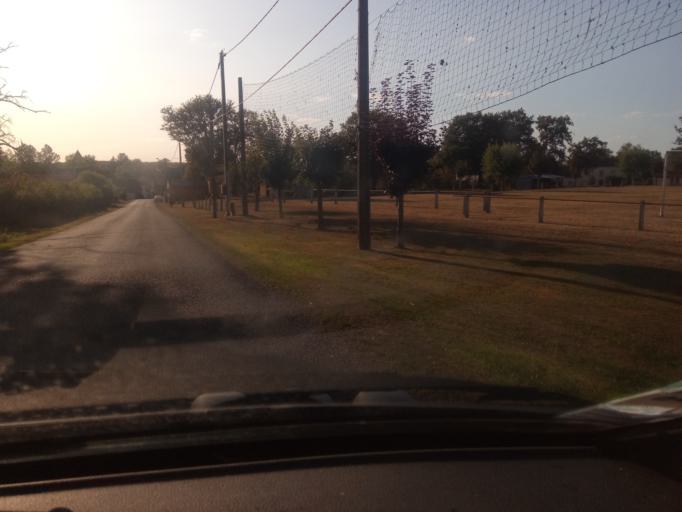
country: FR
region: Poitou-Charentes
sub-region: Departement de la Vienne
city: Availles-Limouzine
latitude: 46.1202
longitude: 0.7862
